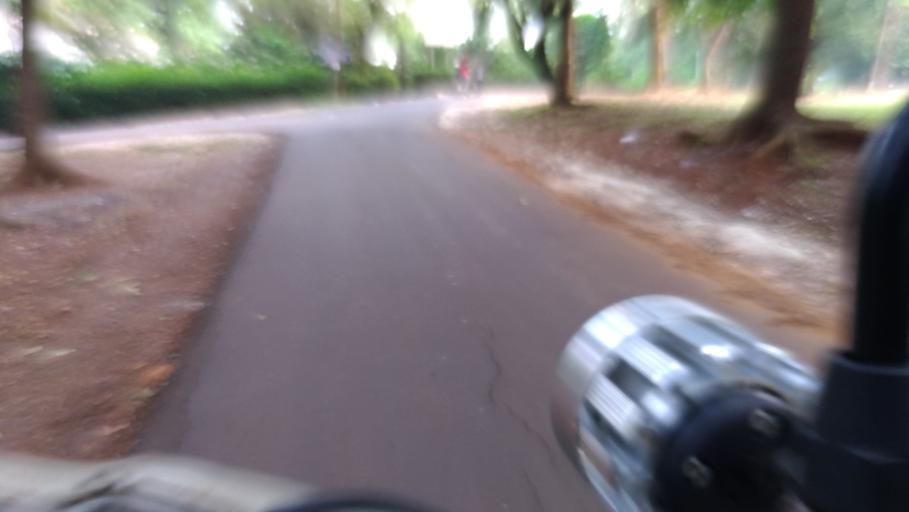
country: ID
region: West Java
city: Cileungsir
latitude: -6.3593
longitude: 106.8975
